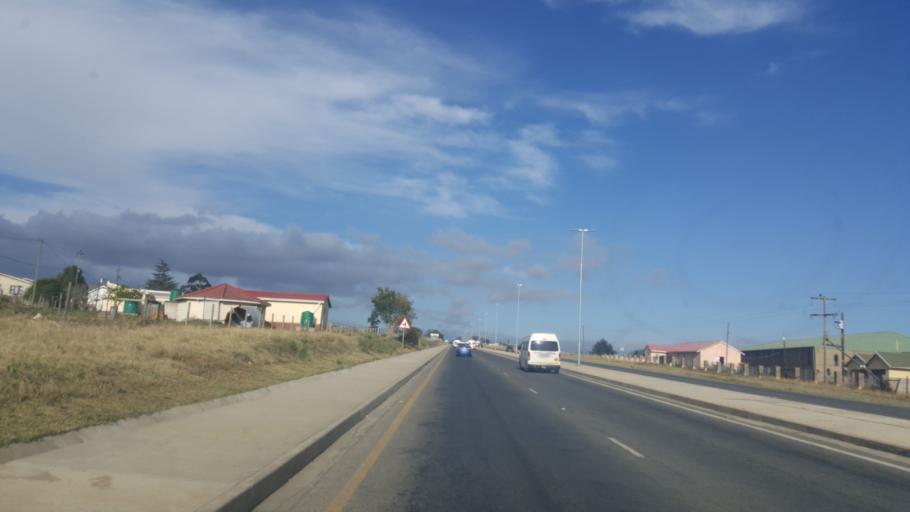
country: ZA
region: Eastern Cape
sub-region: OR Tambo District Municipality
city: Mthatha
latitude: -31.5894
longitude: 28.8328
